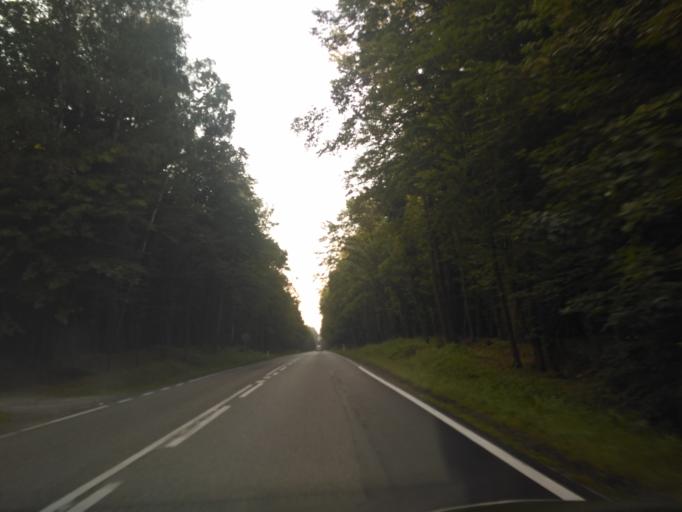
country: PL
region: Lublin Voivodeship
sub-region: Powiat krasnicki
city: Szastarka
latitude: 50.8594
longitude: 22.2811
